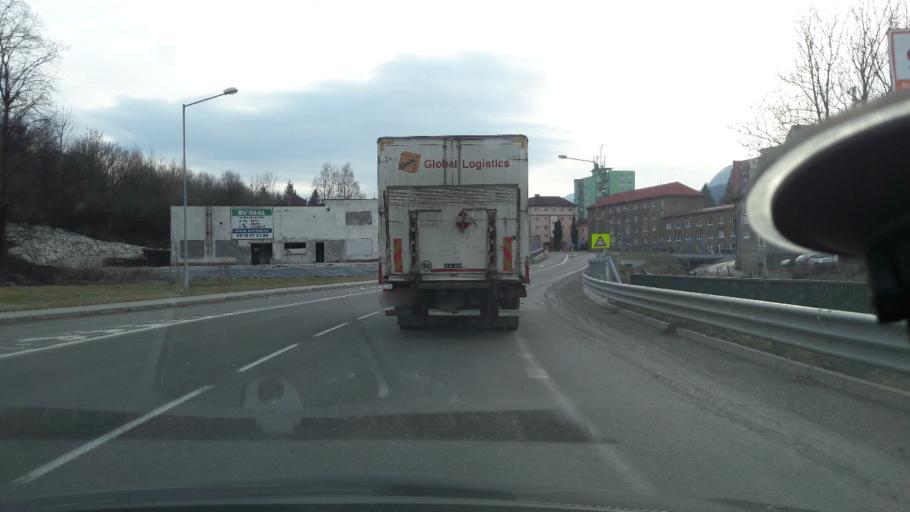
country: SK
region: Nitriansky
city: Handlova
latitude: 48.7271
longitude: 18.7613
